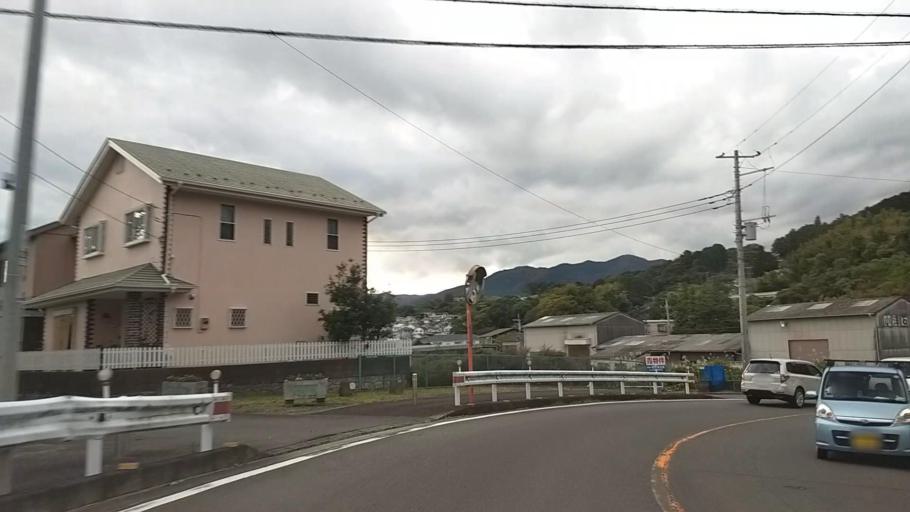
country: JP
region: Kanagawa
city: Yugawara
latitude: 35.1611
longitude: 139.1336
